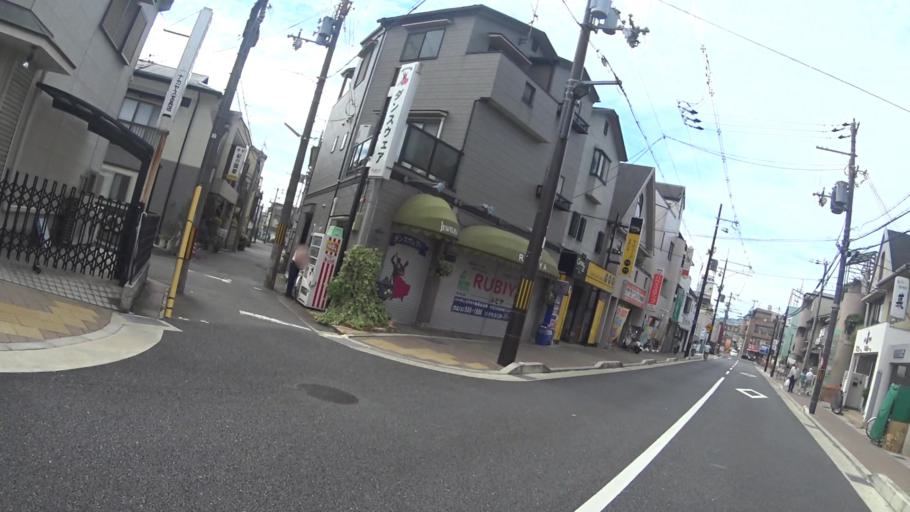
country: JP
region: Kyoto
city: Muko
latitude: 34.9531
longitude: 135.7060
